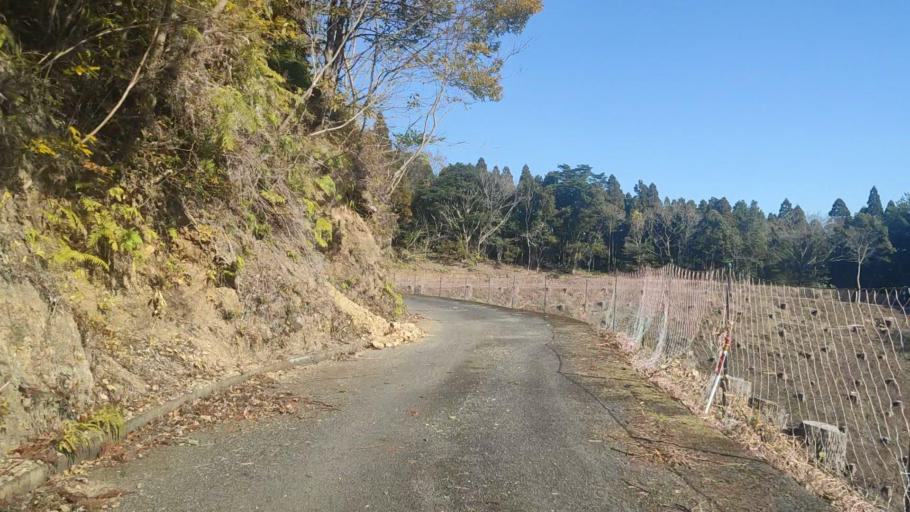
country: JP
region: Oita
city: Saiki
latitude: 32.7833
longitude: 131.8565
